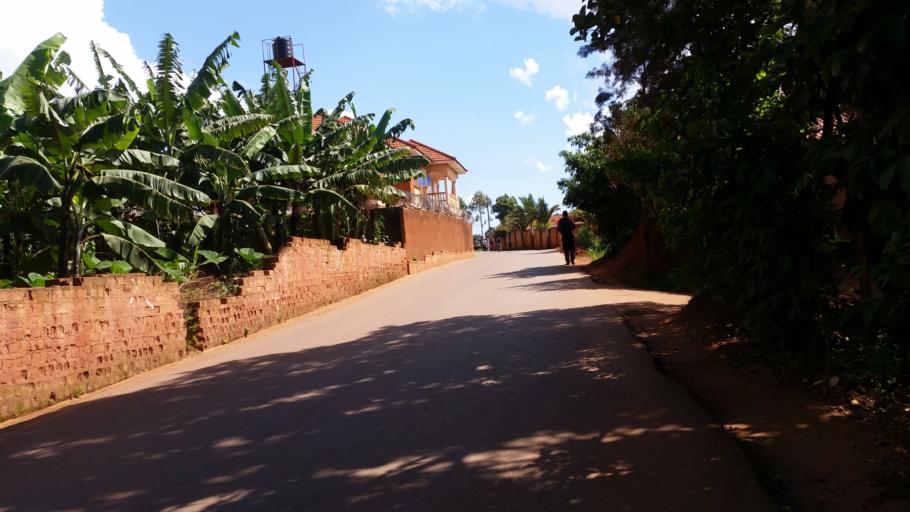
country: UG
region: Central Region
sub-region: Wakiso District
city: Kireka
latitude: 0.3593
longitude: 32.6360
